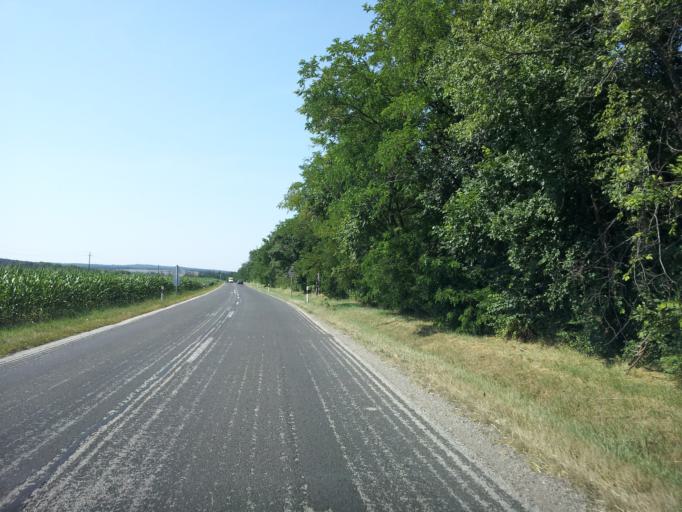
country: HU
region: Fejer
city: Lovasbereny
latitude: 47.2834
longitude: 18.5277
